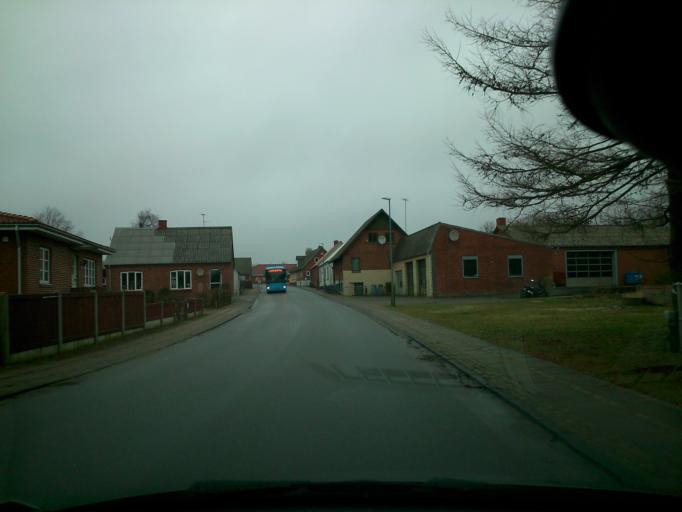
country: DK
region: Central Jutland
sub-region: Ringkobing-Skjern Kommune
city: Skjern
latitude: 56.1106
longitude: 8.4227
